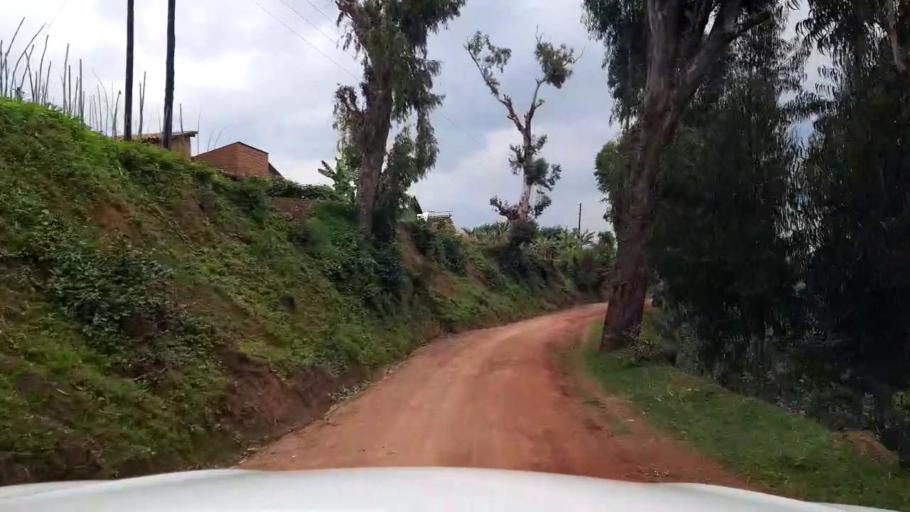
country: RW
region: Northern Province
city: Byumba
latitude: -1.5132
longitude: 29.9417
